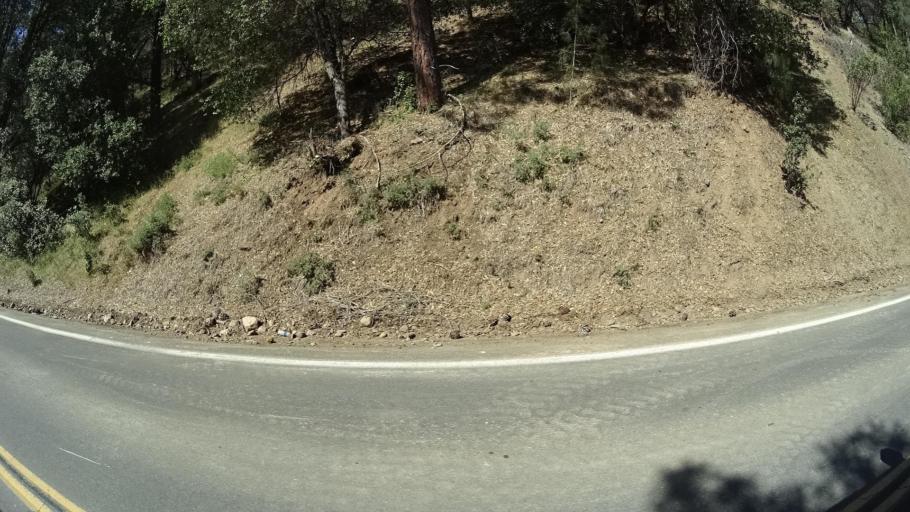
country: US
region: California
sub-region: Lake County
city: Clearlake Oaks
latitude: 39.0453
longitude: -122.5778
